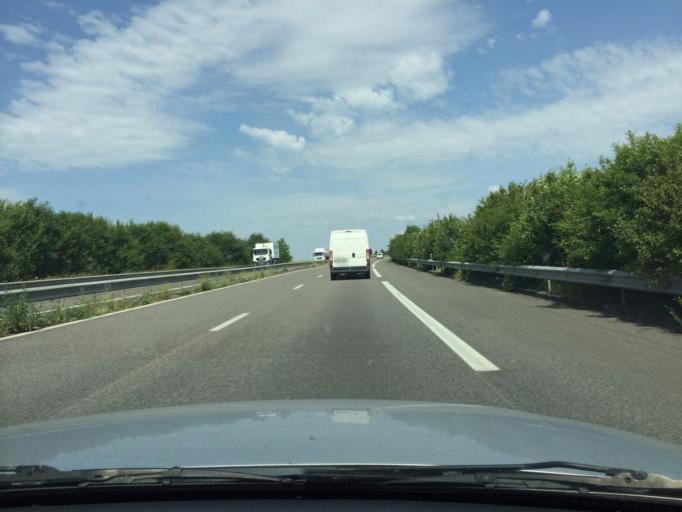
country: FR
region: Lorraine
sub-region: Departement de la Meuse
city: Tronville-en-Barrois
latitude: 48.6545
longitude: 5.2237
